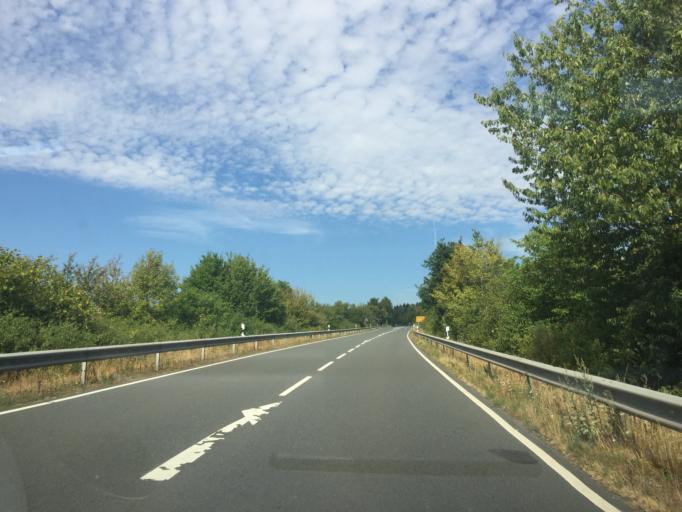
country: DE
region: Lower Saxony
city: Bad Sachsa
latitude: 51.5892
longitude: 10.5478
